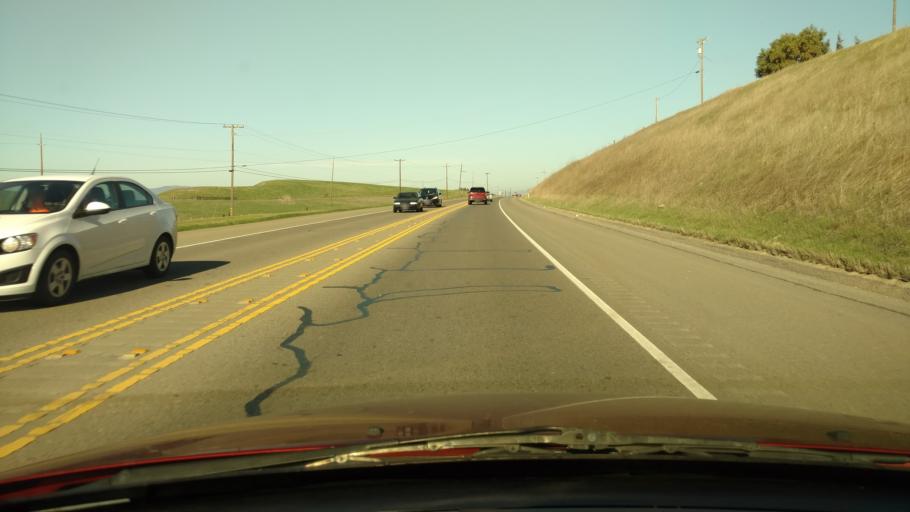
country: US
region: California
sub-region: San Benito County
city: Hollister
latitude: 36.8851
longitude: -121.4181
